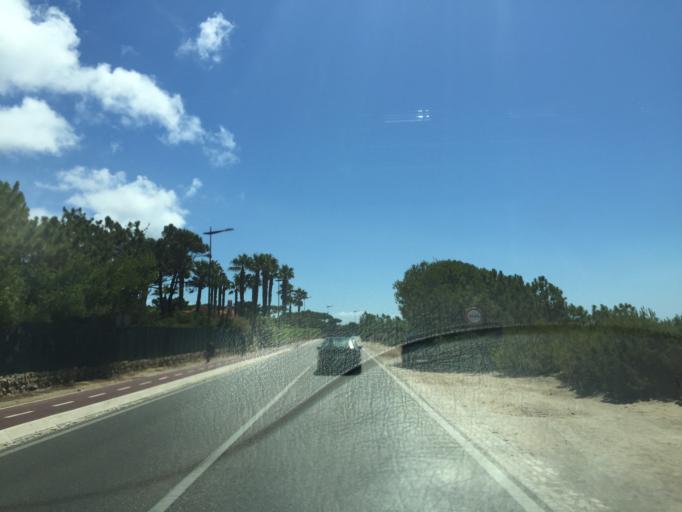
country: PT
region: Lisbon
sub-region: Cascais
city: Cascais
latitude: 38.6974
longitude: -9.4630
